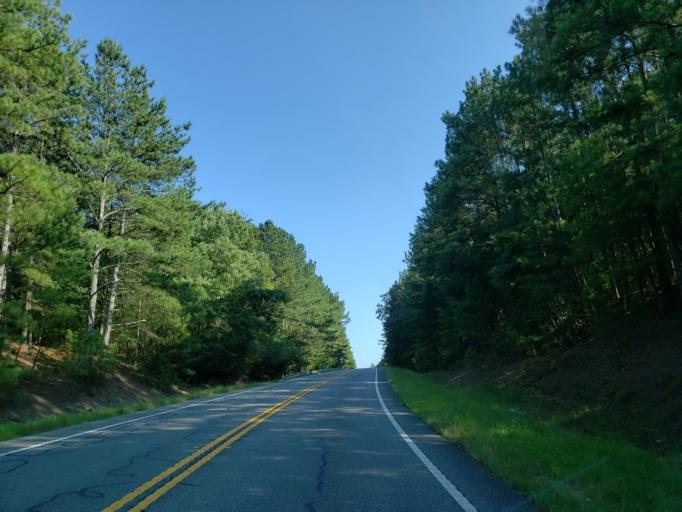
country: US
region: Georgia
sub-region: Whitfield County
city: Varnell
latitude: 34.9025
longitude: -84.9917
